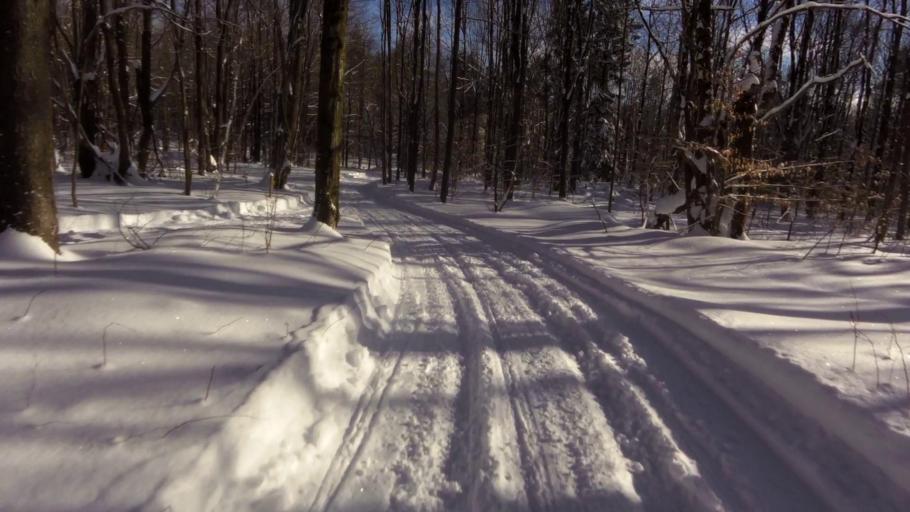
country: US
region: New York
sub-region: Chautauqua County
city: Falconer
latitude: 42.2702
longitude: -79.1413
